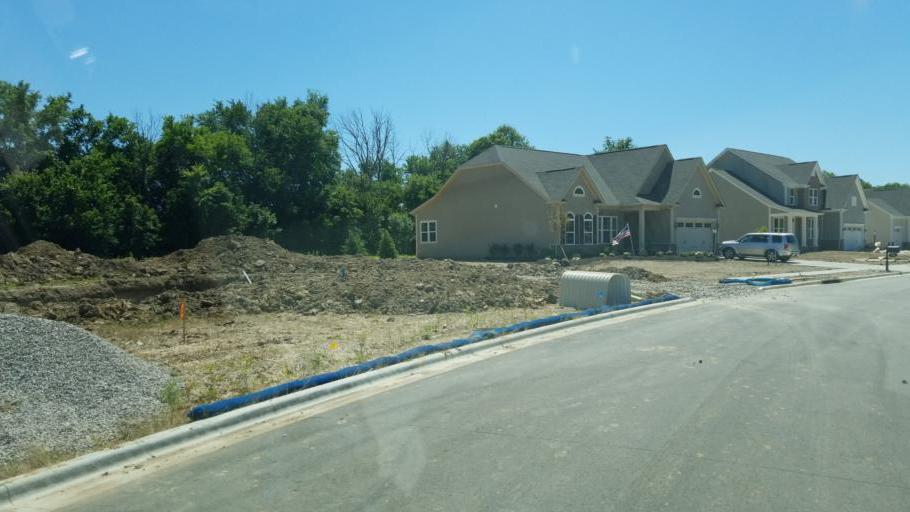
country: US
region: Ohio
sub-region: Franklin County
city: Westerville
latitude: 40.1879
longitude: -82.9038
